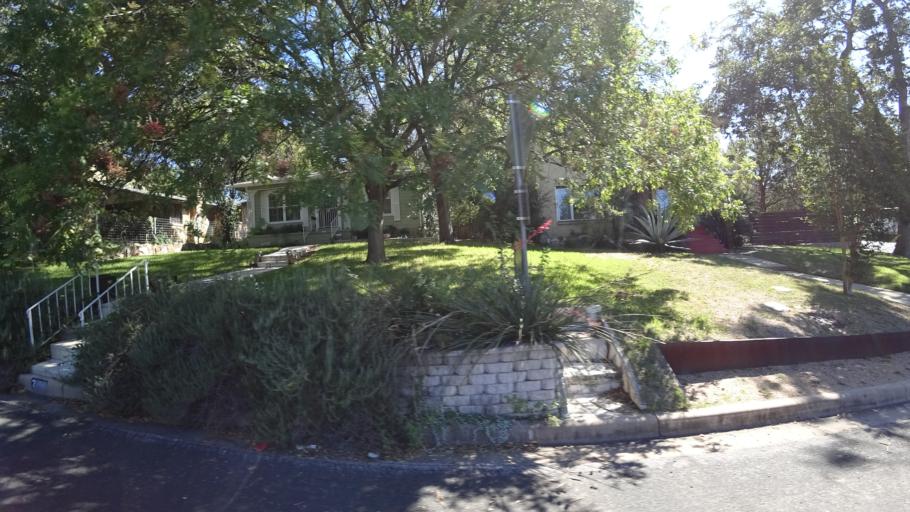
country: US
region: Texas
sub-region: Travis County
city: Austin
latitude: 30.2381
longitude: -97.7452
